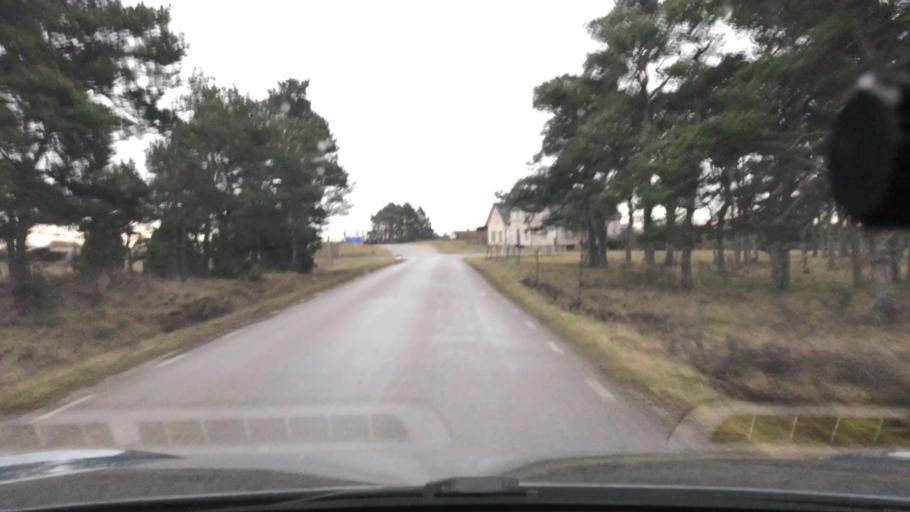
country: SE
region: Gotland
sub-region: Gotland
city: Slite
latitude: 57.3995
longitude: 18.8054
